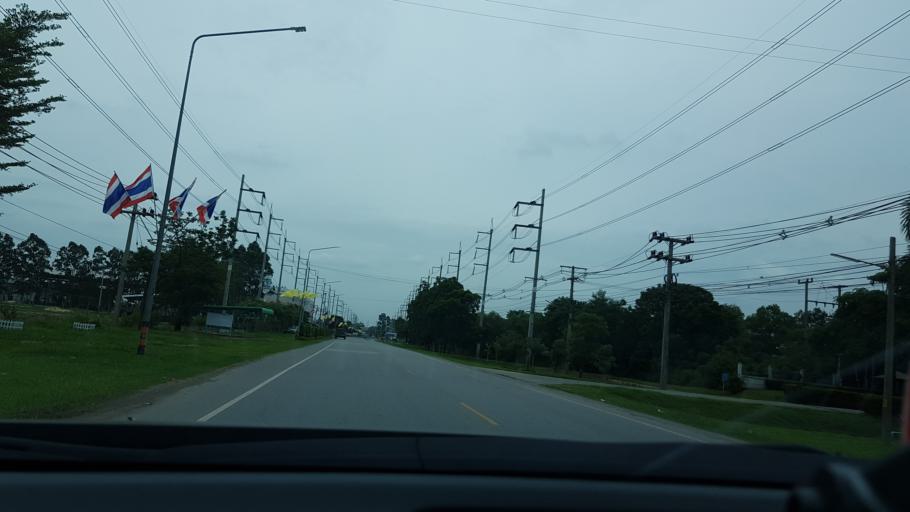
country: TH
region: Phra Nakhon Si Ayutthaya
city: Bang Pa-in
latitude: 14.1684
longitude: 100.5261
